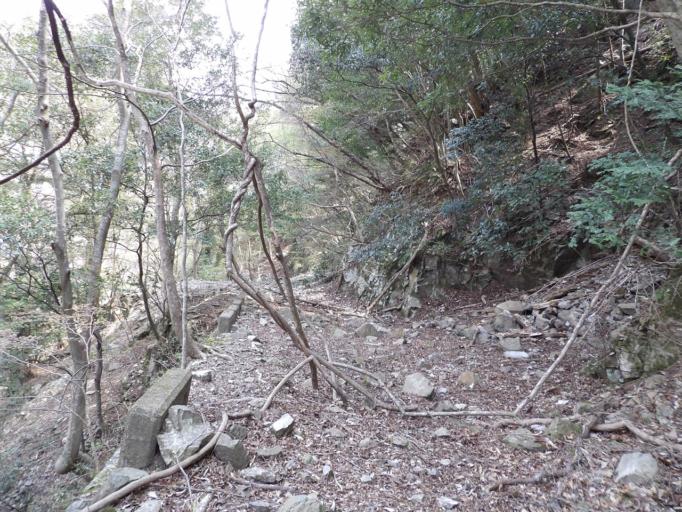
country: JP
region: Shizuoka
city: Mori
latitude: 35.1483
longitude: 137.8253
